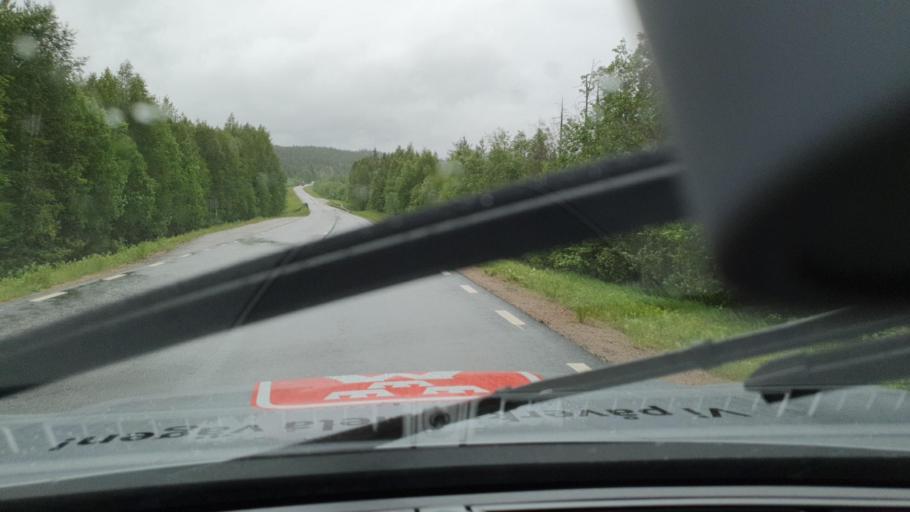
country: SE
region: Norrbotten
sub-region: Overtornea Kommun
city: OEvertornea
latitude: 66.4406
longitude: 23.3189
